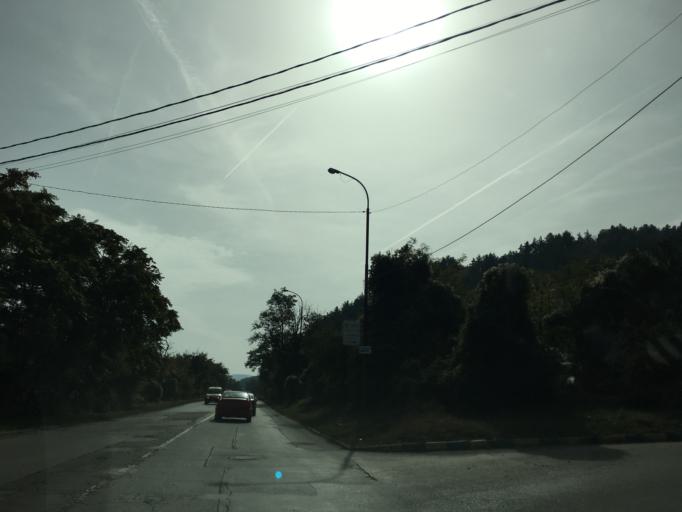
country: BG
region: Sofia-Capital
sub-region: Stolichna Obshtina
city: Sofia
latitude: 42.6076
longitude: 23.4003
